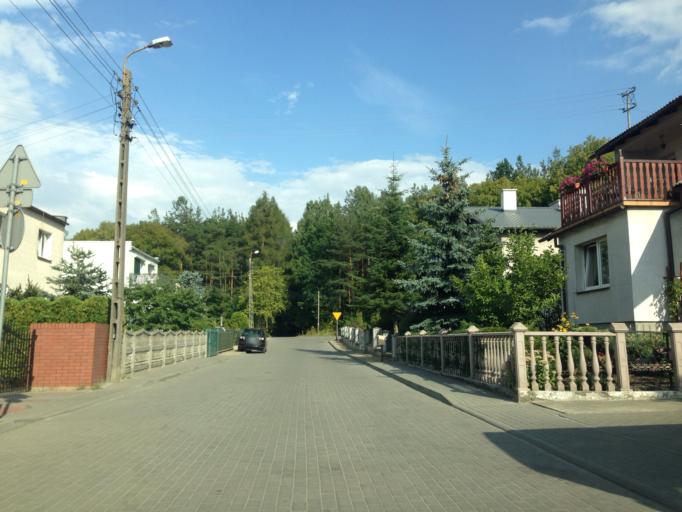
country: PL
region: Kujawsko-Pomorskie
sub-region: Powiat swiecki
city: Swiekatowo
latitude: 53.4859
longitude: 18.1339
